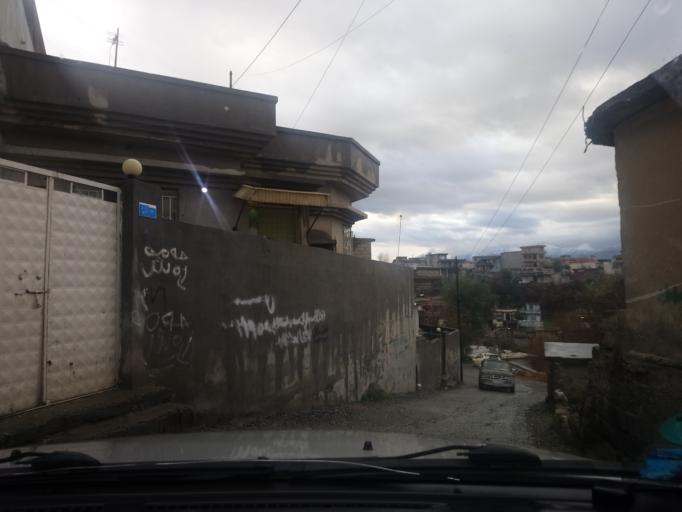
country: IQ
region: As Sulaymaniyah
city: Qeladize
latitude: 36.1822
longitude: 45.1218
